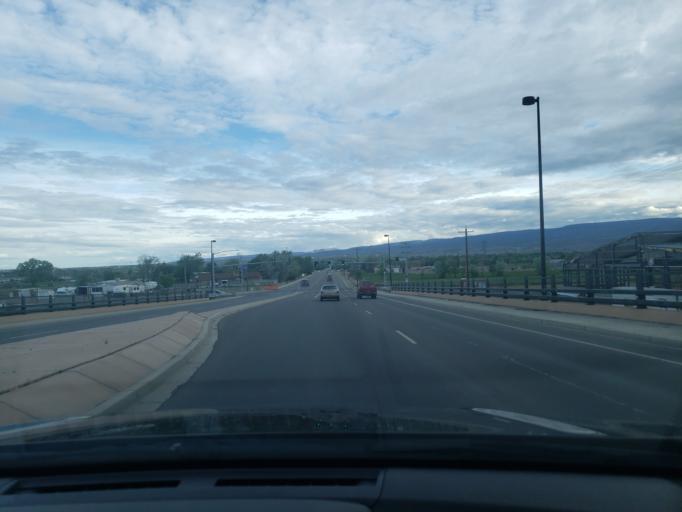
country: US
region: Colorado
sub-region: Mesa County
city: Fruitvale
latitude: 39.0699
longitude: -108.5153
